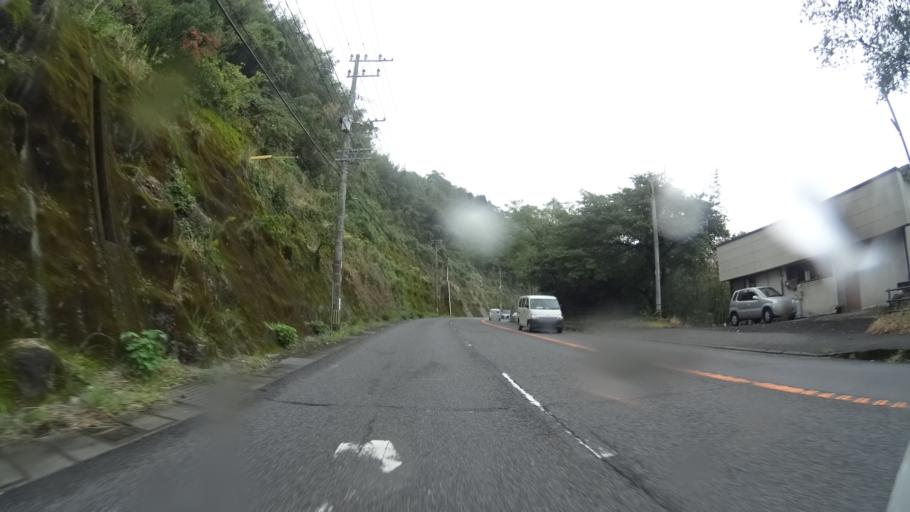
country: JP
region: Kagoshima
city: Kajiki
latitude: 31.7489
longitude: 130.6713
